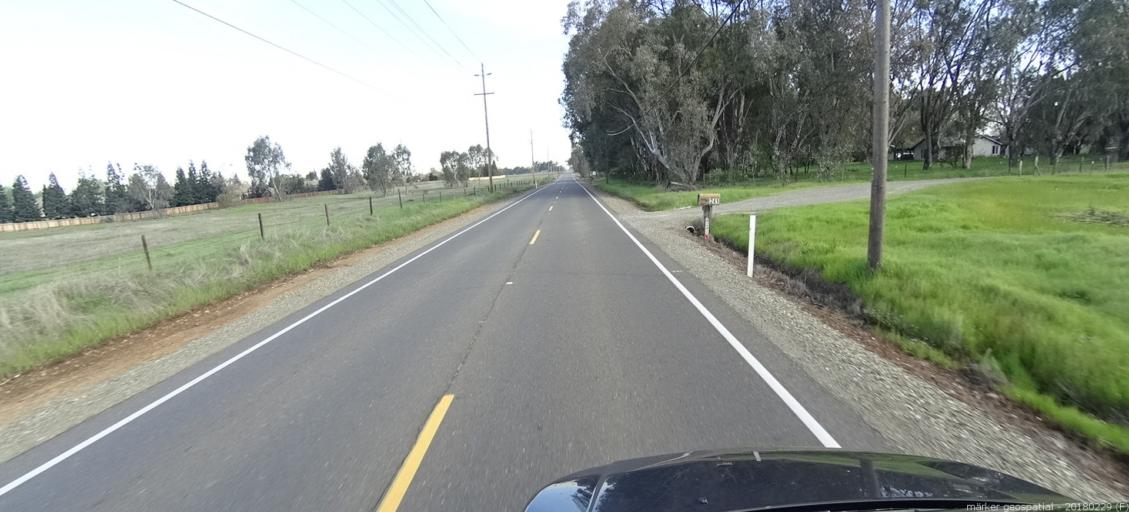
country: US
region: California
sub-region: Sacramento County
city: Vineyard
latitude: 38.4582
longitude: -121.2975
